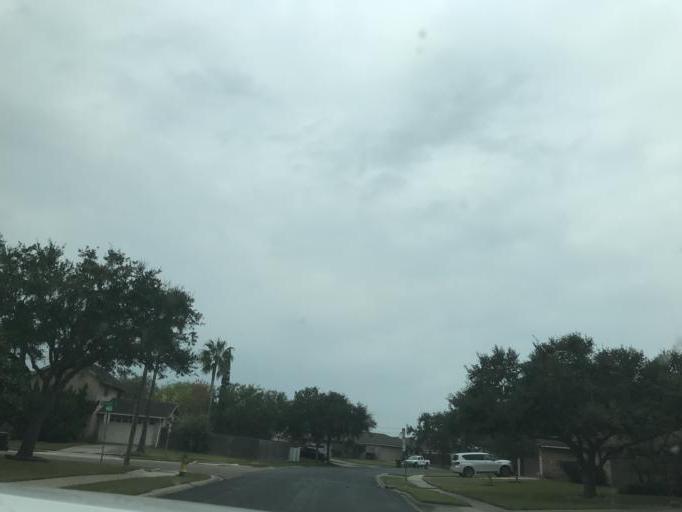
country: US
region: Texas
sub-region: Nueces County
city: Corpus Christi
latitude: 27.6724
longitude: -97.3488
